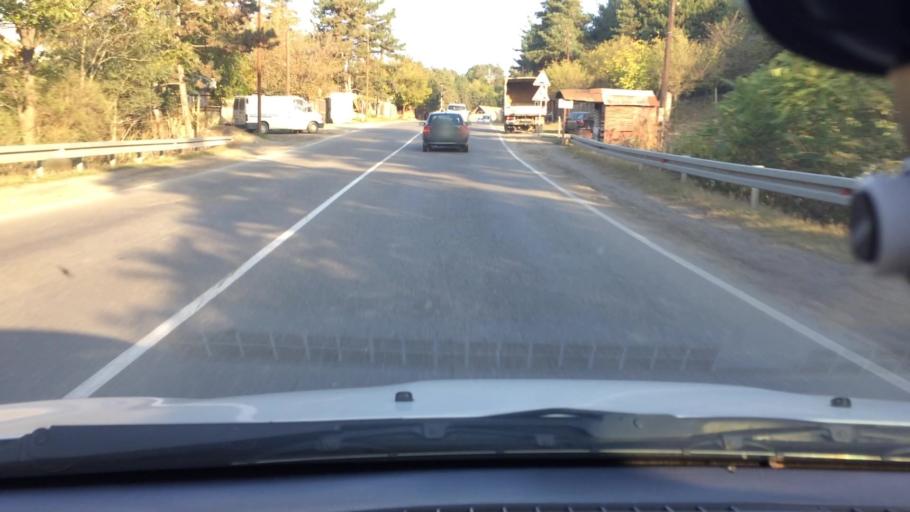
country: GE
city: Surami
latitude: 42.0255
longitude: 43.5624
